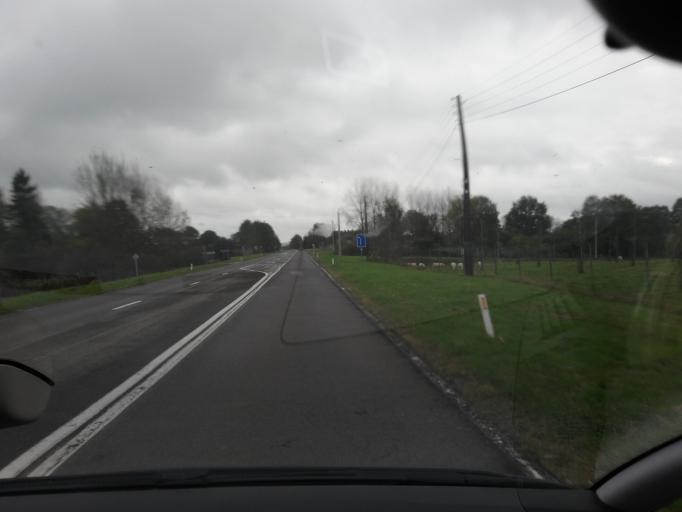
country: BE
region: Wallonia
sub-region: Province du Luxembourg
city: Habay-la-Vieille
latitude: 49.7153
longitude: 5.6874
